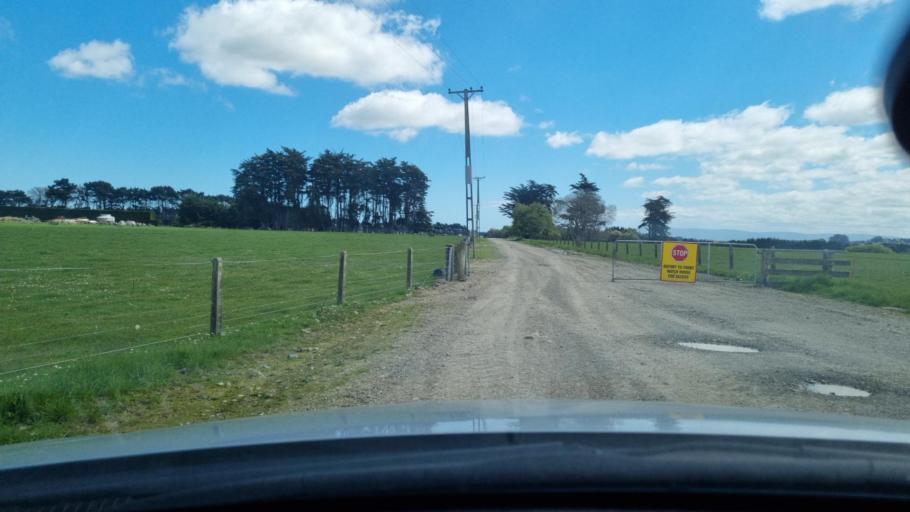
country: NZ
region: Southland
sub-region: Invercargill City
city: Invercargill
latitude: -46.3510
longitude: 168.3088
